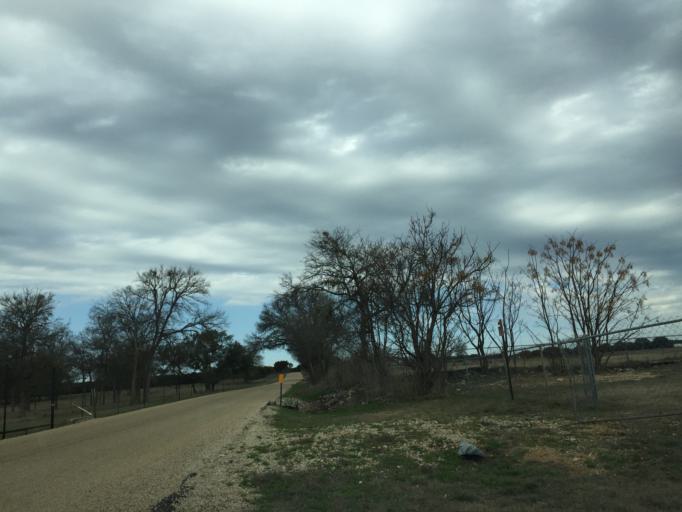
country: US
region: Texas
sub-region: Burnet County
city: Bertram
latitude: 30.6468
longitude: -98.0133
